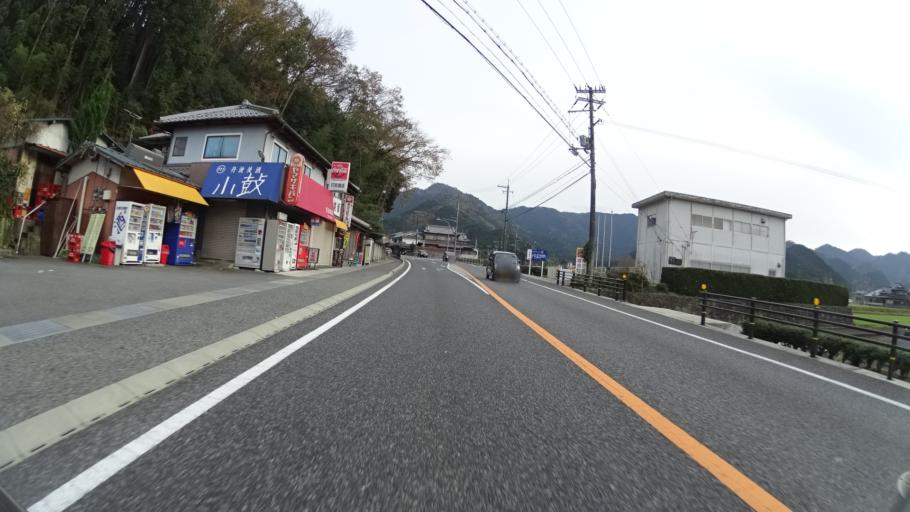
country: JP
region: Hyogo
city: Sasayama
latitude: 35.1189
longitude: 135.0884
